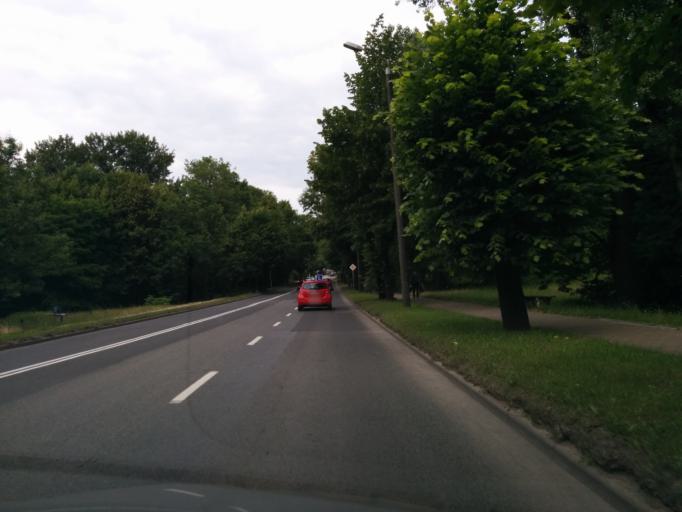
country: PL
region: Silesian Voivodeship
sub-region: Ruda Slaska
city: Ruda Slaska
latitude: 50.2724
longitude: 18.8466
